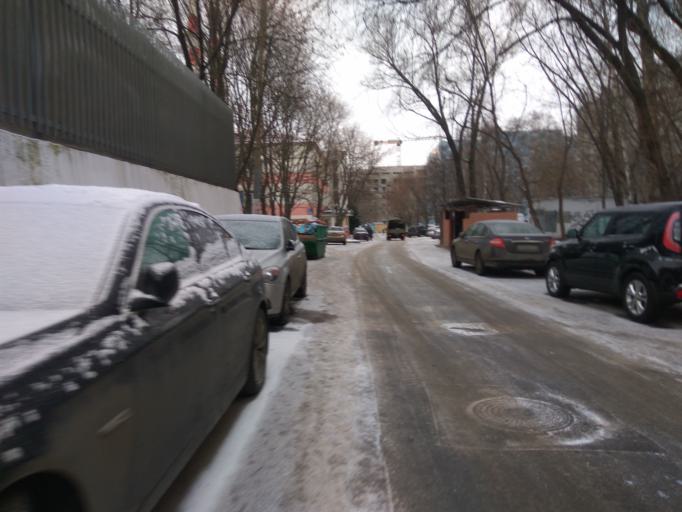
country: RU
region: Moscow
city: Kolomenskoye
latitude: 55.6740
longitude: 37.6607
